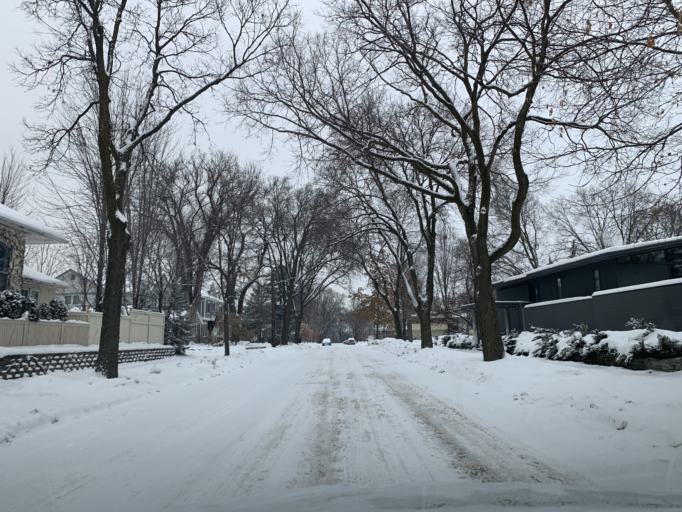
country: US
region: Minnesota
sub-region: Hennepin County
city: Saint Louis Park
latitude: 44.9517
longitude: -93.3250
